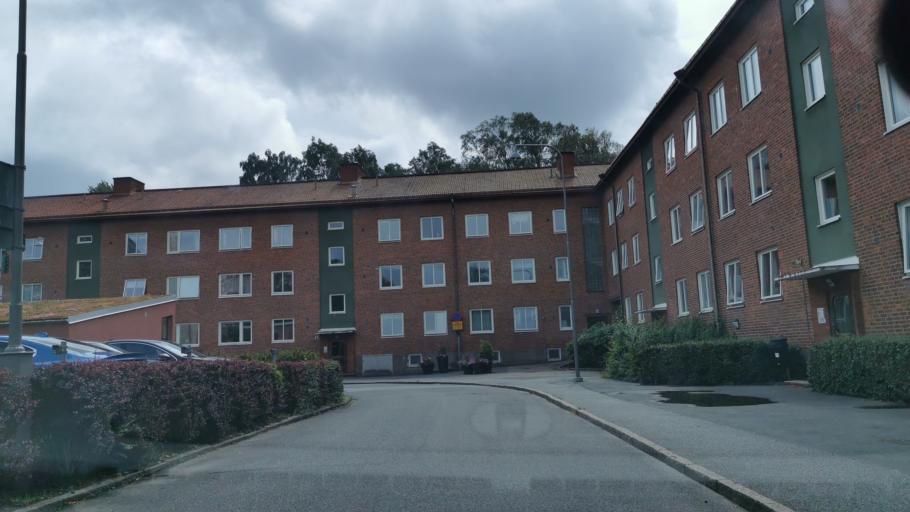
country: SE
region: Vaestra Goetaland
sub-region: Goteborg
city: Goeteborg
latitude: 57.6816
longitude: 11.9760
